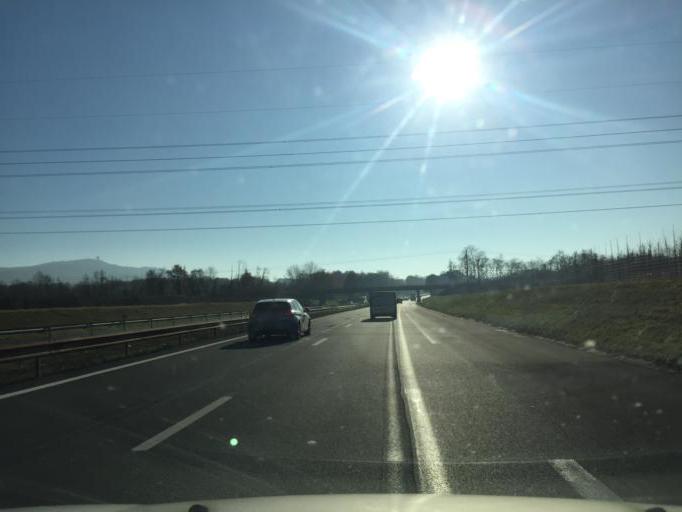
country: FR
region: Rhone-Alpes
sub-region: Departement du Rhone
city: Les Cheres
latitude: 45.8822
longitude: 4.7385
